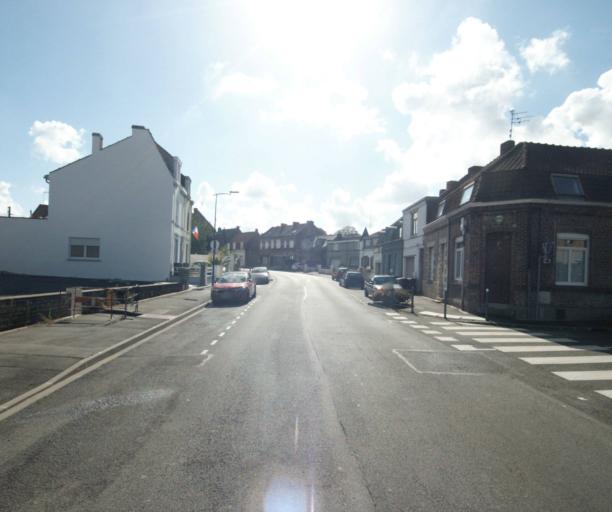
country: FR
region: Nord-Pas-de-Calais
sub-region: Departement du Nord
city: Lys-lez-Lannoy
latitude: 50.6608
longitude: 3.2228
